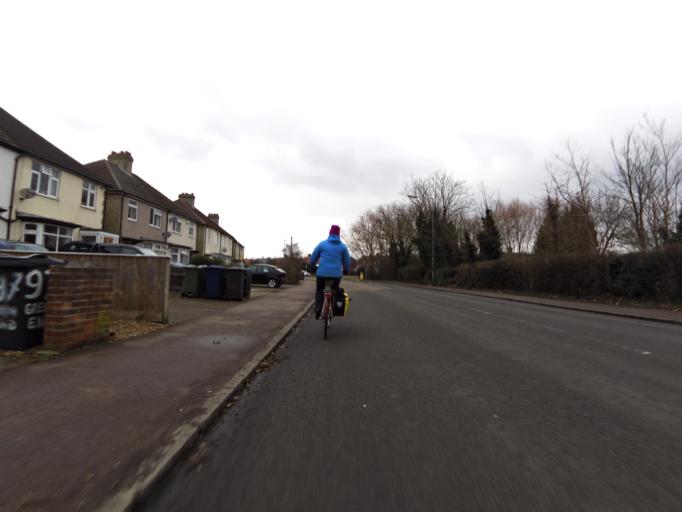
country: GB
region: England
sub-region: Cambridgeshire
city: Cambridge
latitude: 52.2236
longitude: 0.1485
